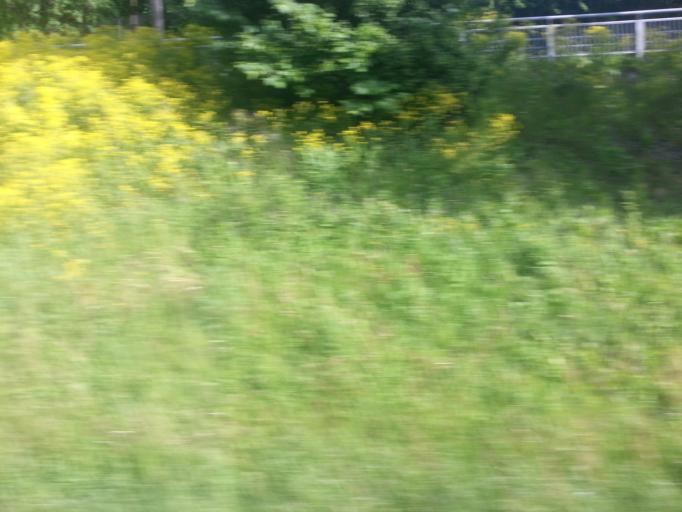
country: NO
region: Akershus
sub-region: Baerum
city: Sandvika
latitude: 59.8934
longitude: 10.5428
